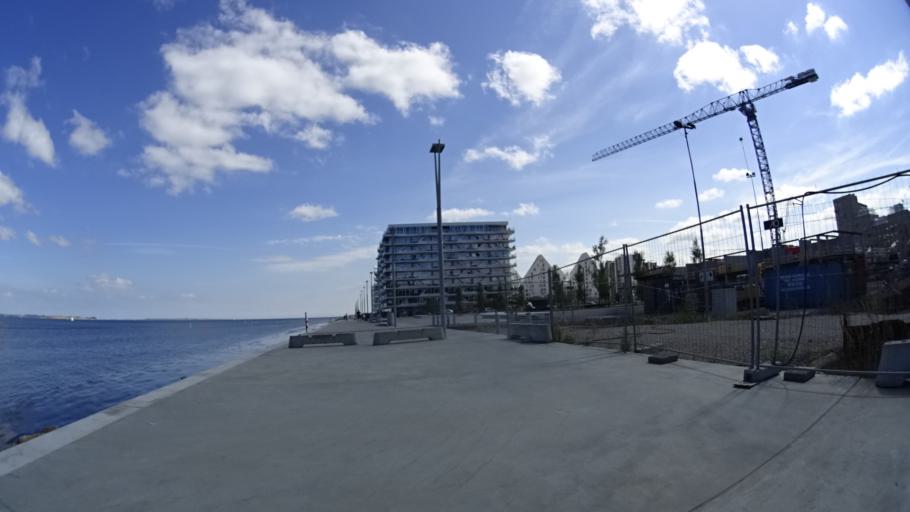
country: DK
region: Central Jutland
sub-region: Arhus Kommune
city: Arhus
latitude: 56.1682
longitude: 10.2273
